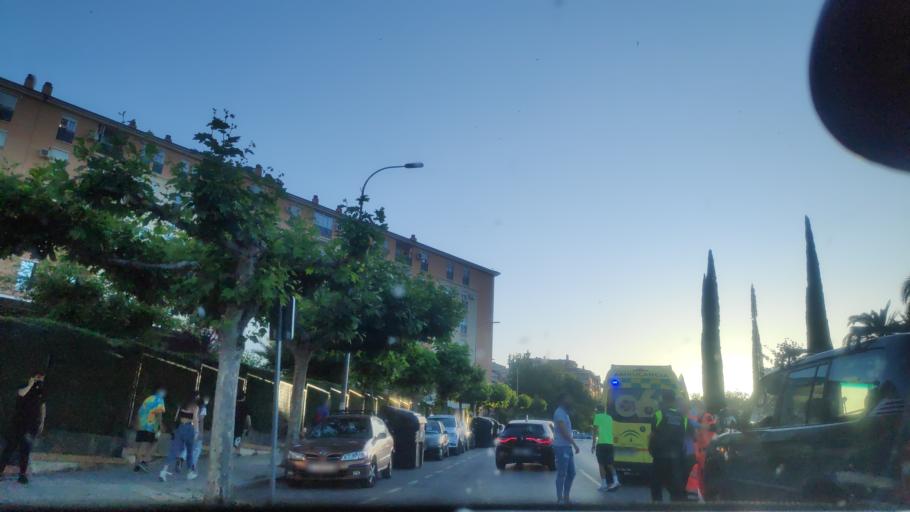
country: ES
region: Andalusia
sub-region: Provincia de Jaen
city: Jaen
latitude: 37.7823
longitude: -3.8092
